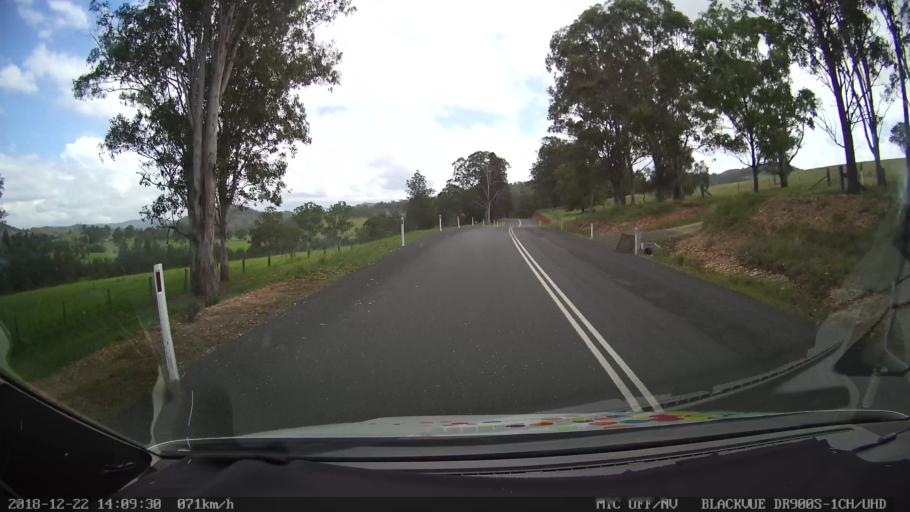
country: AU
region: New South Wales
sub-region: Clarence Valley
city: Coutts Crossing
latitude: -29.9868
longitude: 152.7169
